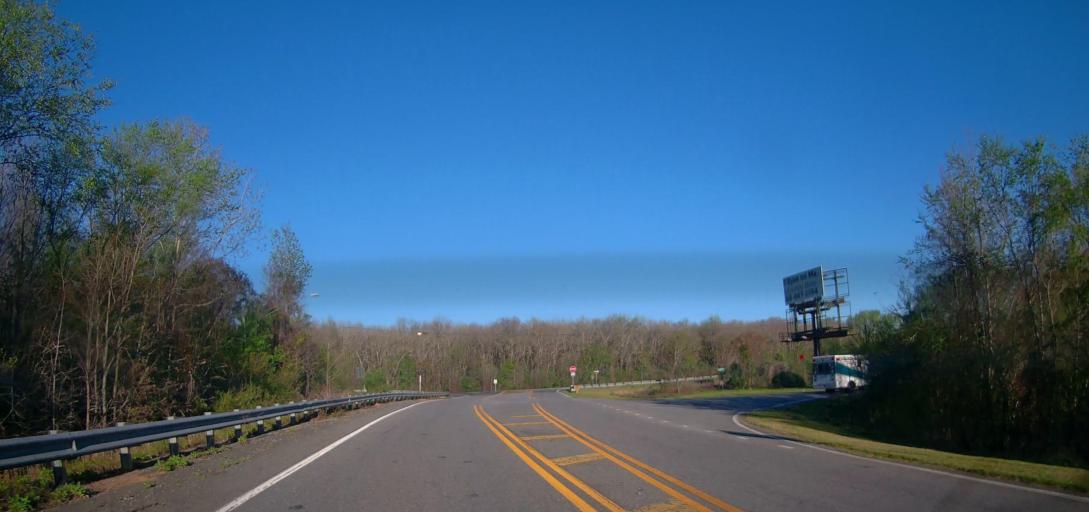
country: US
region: Georgia
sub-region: Wilkinson County
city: Irwinton
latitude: 32.8488
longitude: -83.1944
